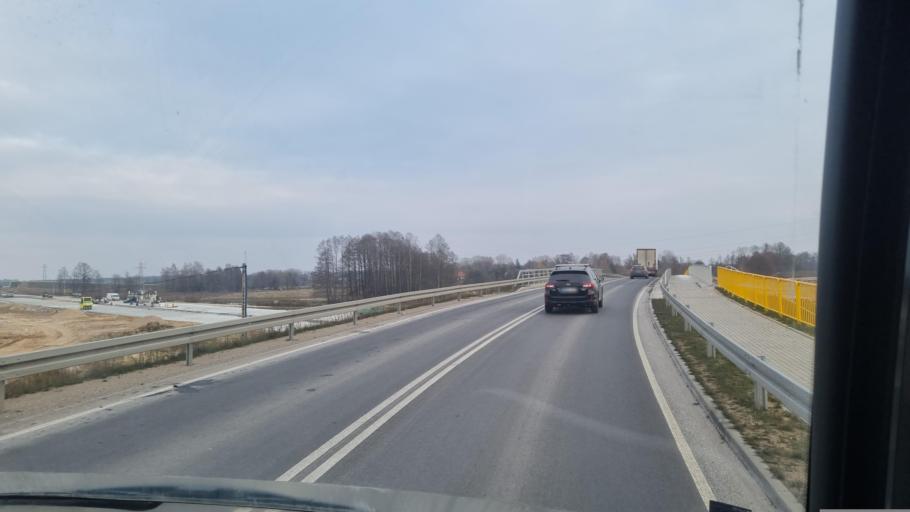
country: PL
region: Warmian-Masurian Voivodeship
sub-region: Powiat elcki
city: Elk
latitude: 53.8480
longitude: 22.4595
